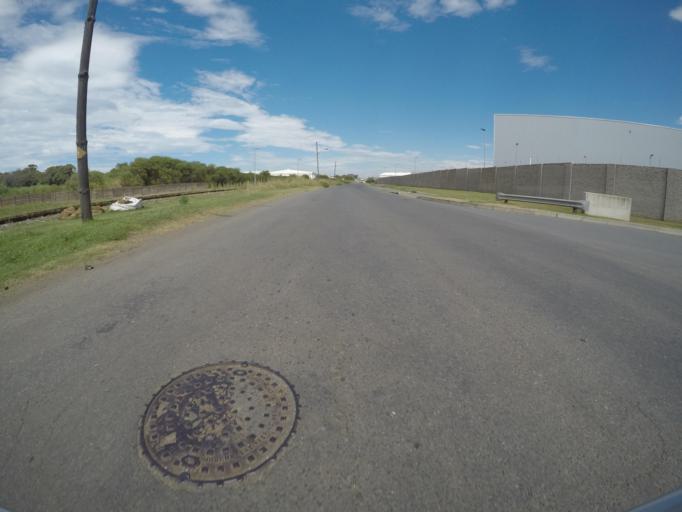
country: ZA
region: Eastern Cape
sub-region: Buffalo City Metropolitan Municipality
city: East London
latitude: -33.0333
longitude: 27.8919
